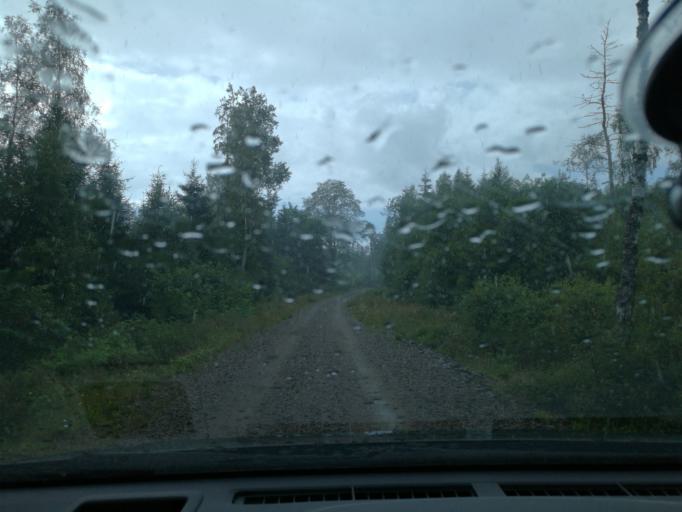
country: SE
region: Kronoberg
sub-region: Alvesta Kommun
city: Vislanda
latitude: 56.7052
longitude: 14.4111
